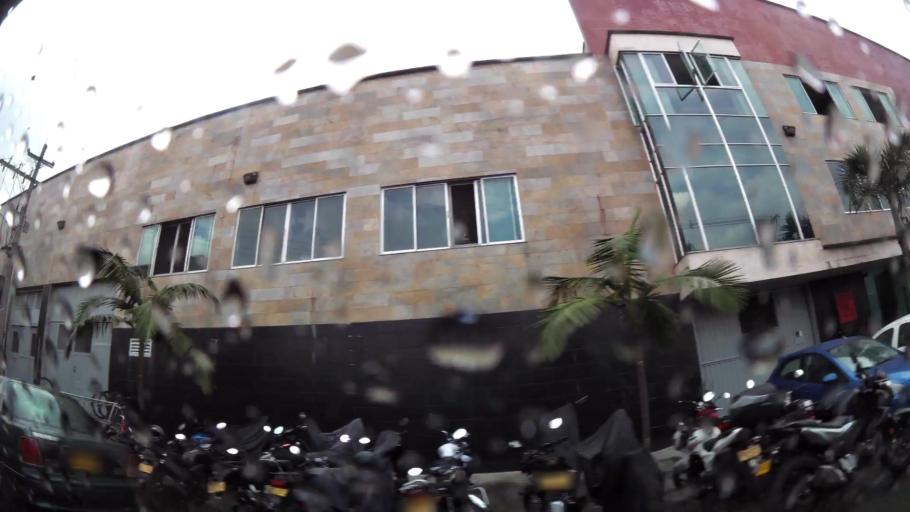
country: CO
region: Antioquia
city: Itagui
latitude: 6.1841
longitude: -75.5923
